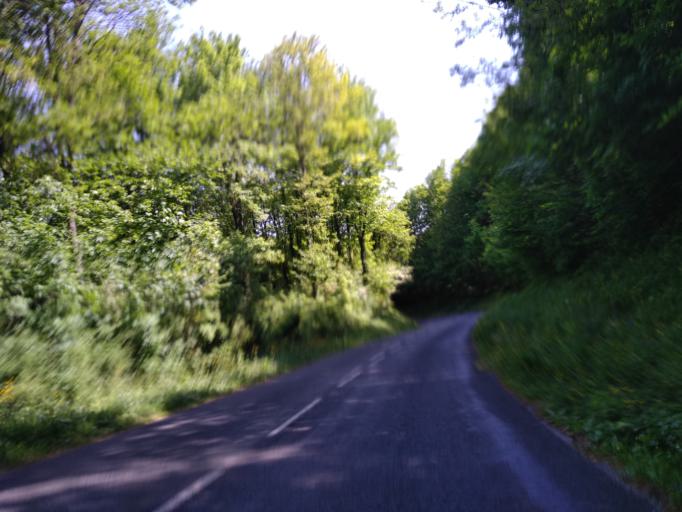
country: FR
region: Rhone-Alpes
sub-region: Departement du Rhone
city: Limonest
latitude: 45.8315
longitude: 4.8019
